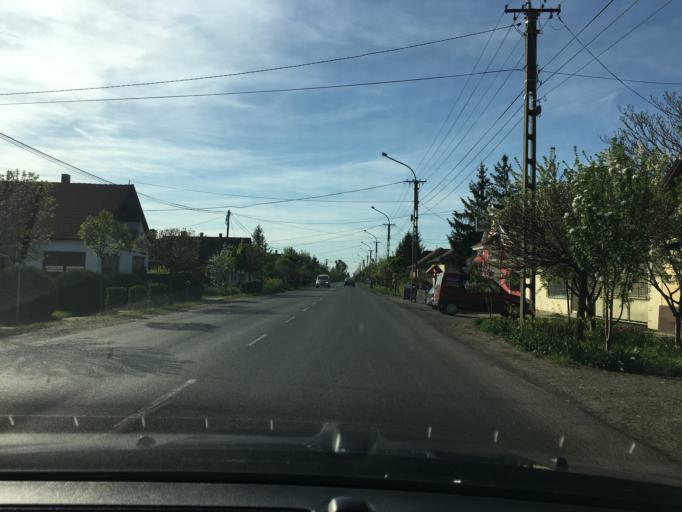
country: HU
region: Bekes
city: Korostarcsa
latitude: 46.8733
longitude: 21.0224
